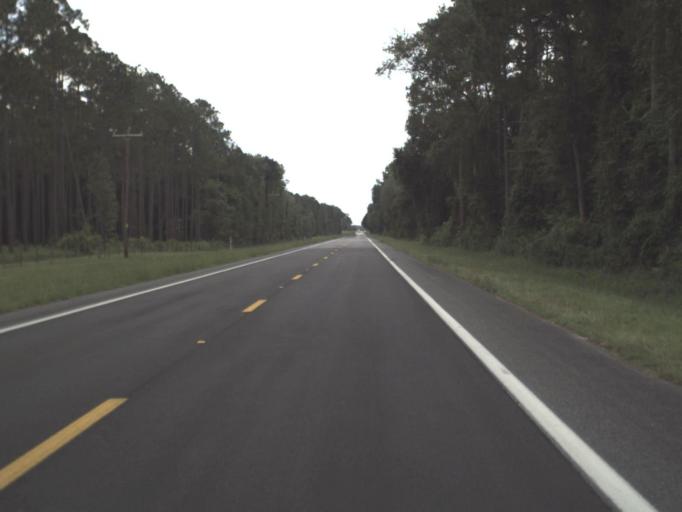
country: US
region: Florida
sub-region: Union County
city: Lake Butler
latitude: 30.0430
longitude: -82.3890
